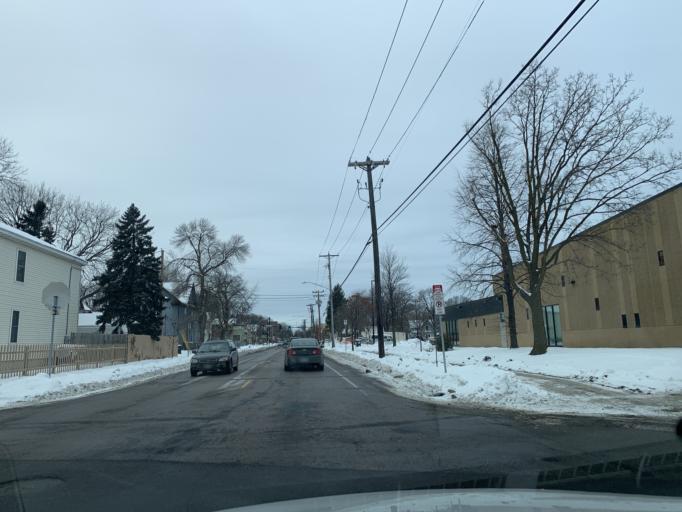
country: US
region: Minnesota
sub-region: Hennepin County
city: Minneapolis
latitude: 44.9592
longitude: -93.2561
